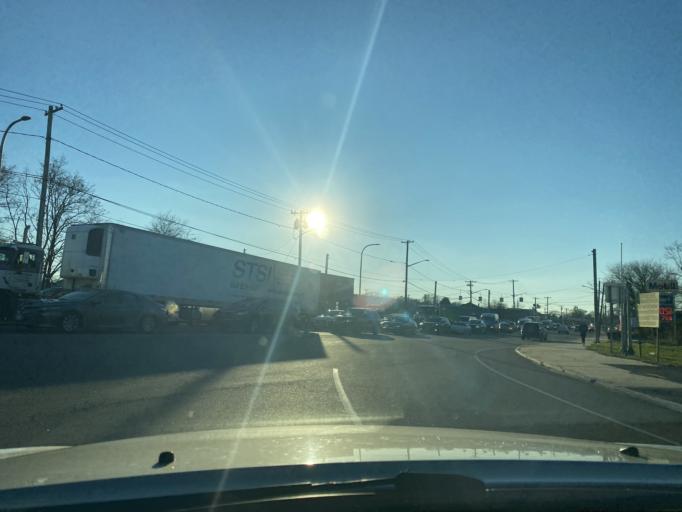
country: US
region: New York
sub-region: Nassau County
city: Inwood
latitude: 40.6232
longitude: -73.7411
